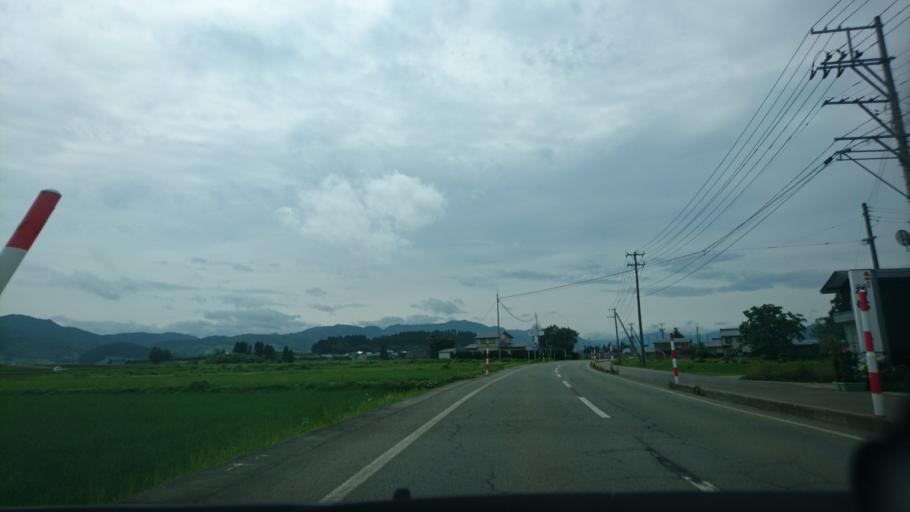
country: JP
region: Akita
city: Yuzawa
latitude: 39.1902
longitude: 140.5508
